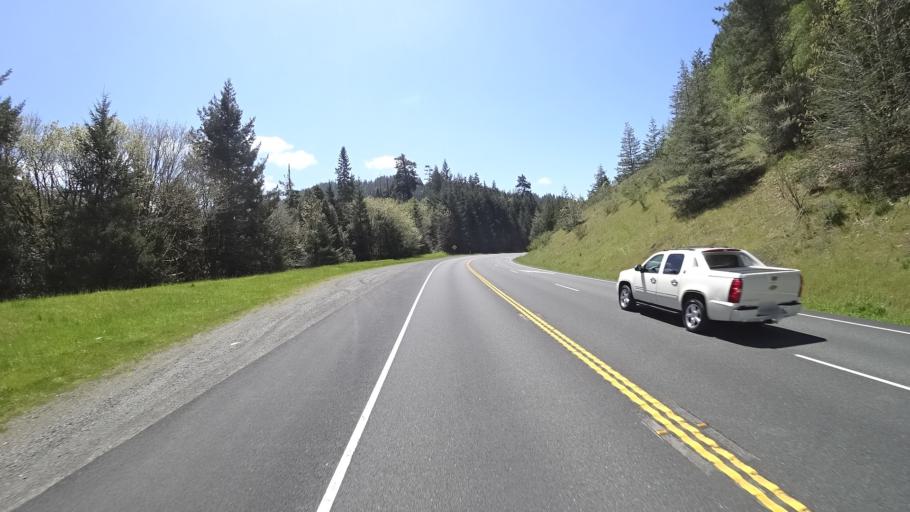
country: US
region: California
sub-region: Humboldt County
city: Blue Lake
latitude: 40.9021
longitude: -123.9173
